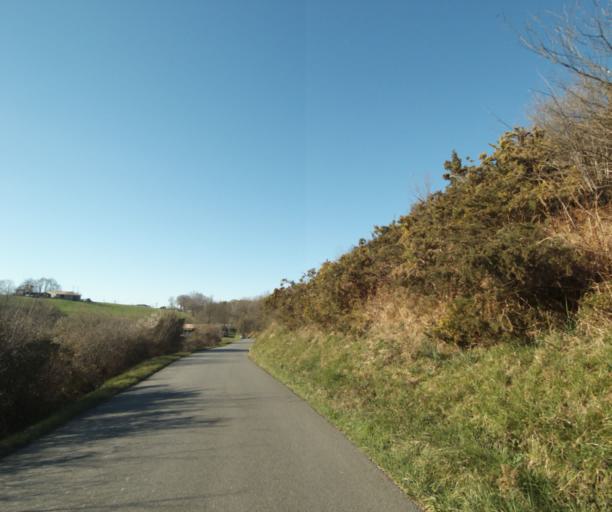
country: FR
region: Aquitaine
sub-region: Departement des Pyrenees-Atlantiques
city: Hendaye
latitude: 43.3574
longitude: -1.7516
